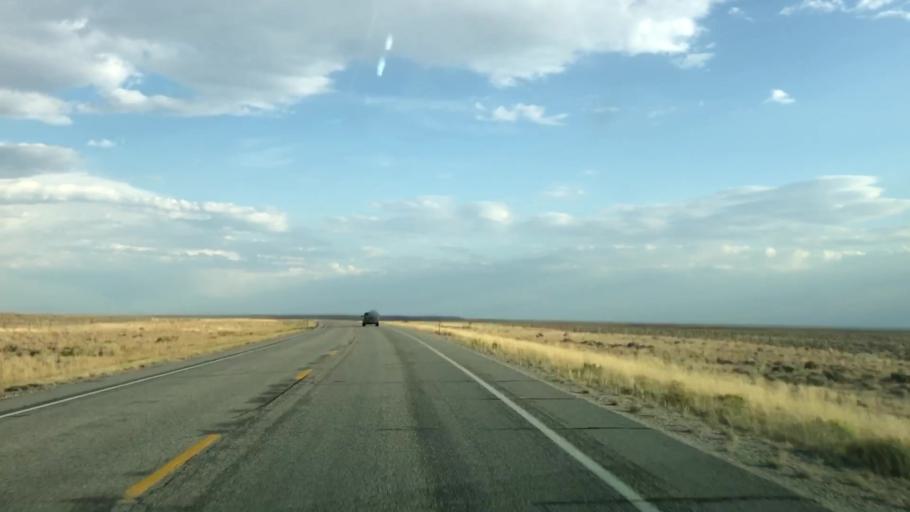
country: US
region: Wyoming
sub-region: Sublette County
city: Marbleton
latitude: 42.3369
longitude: -109.5203
